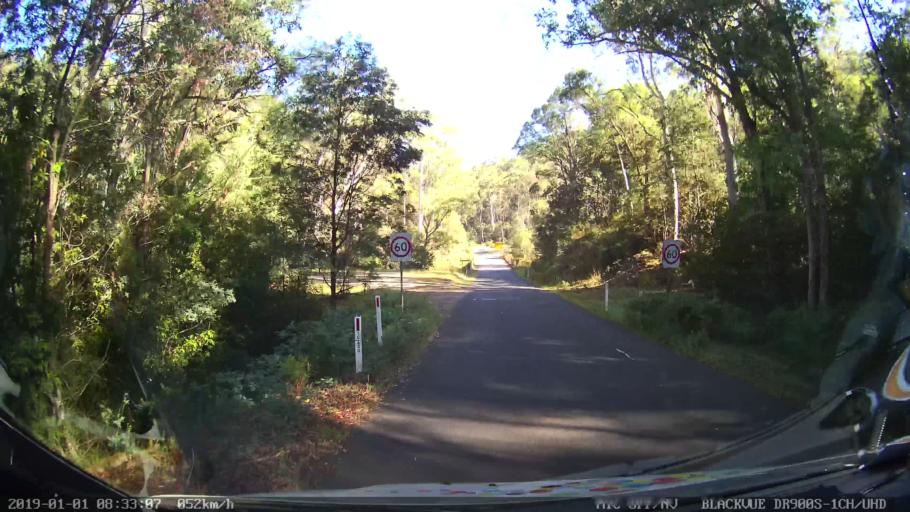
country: AU
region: New South Wales
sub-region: Snowy River
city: Jindabyne
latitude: -36.3572
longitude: 148.2034
